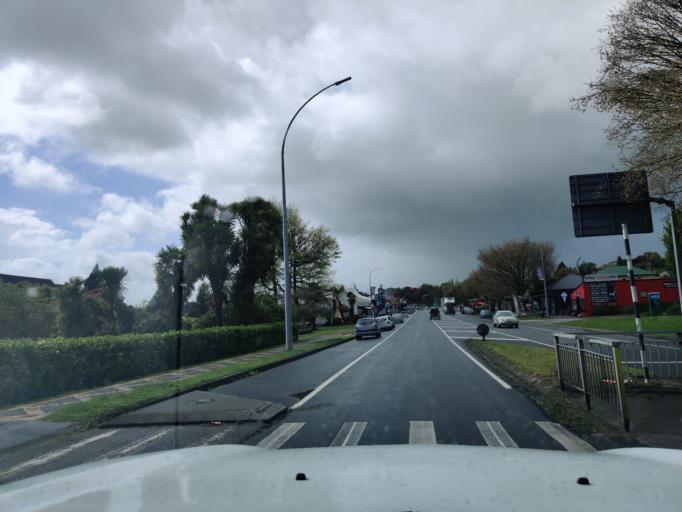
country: NZ
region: Waikato
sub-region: Matamata-Piako District
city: Matamata
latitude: -37.9763
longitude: 175.7554
